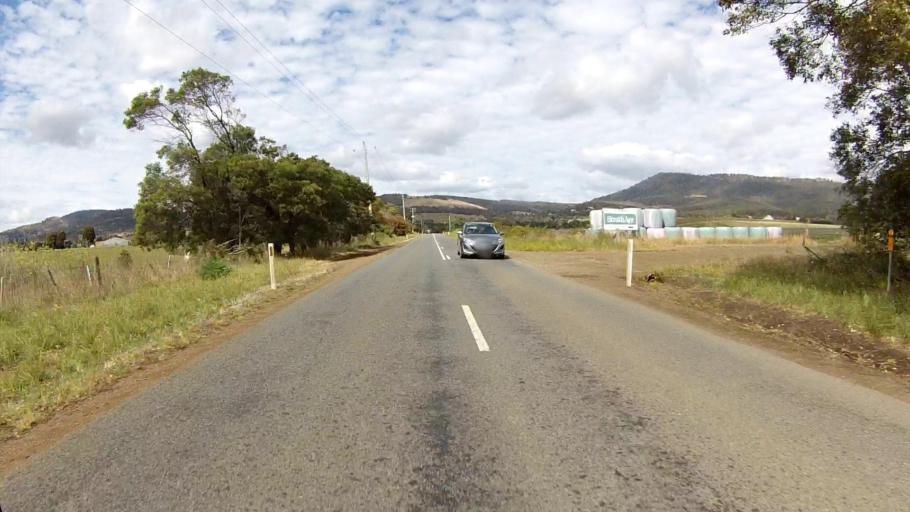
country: AU
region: Tasmania
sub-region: Clarence
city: Cambridge
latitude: -42.7540
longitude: 147.4078
